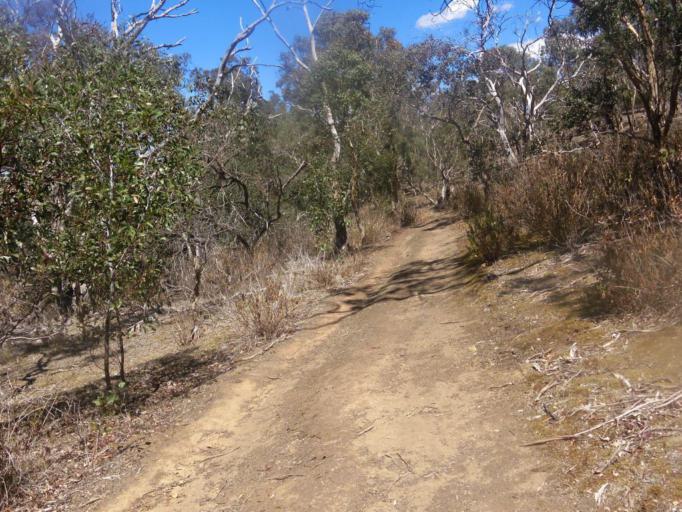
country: AU
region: Victoria
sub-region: Moorabool
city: Bacchus Marsh
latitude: -37.6607
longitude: 144.3574
